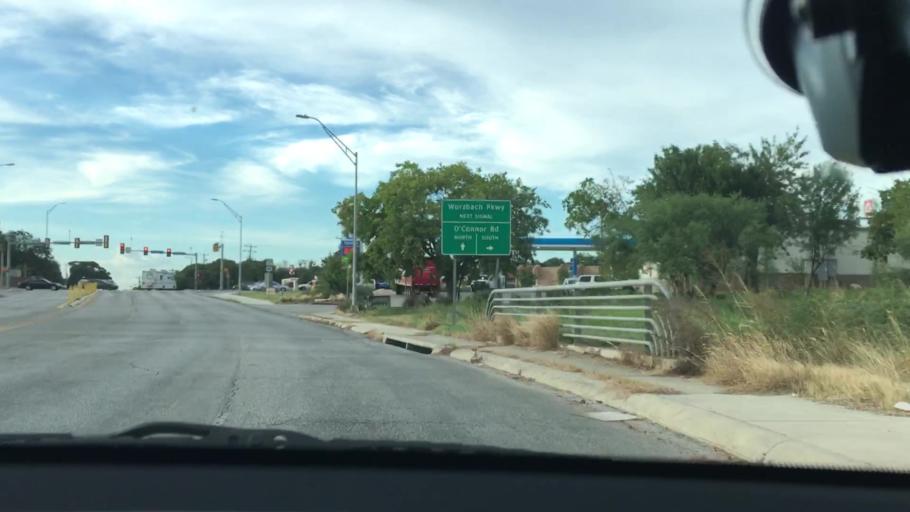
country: US
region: Texas
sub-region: Bexar County
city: Windcrest
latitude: 29.5478
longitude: -98.3749
